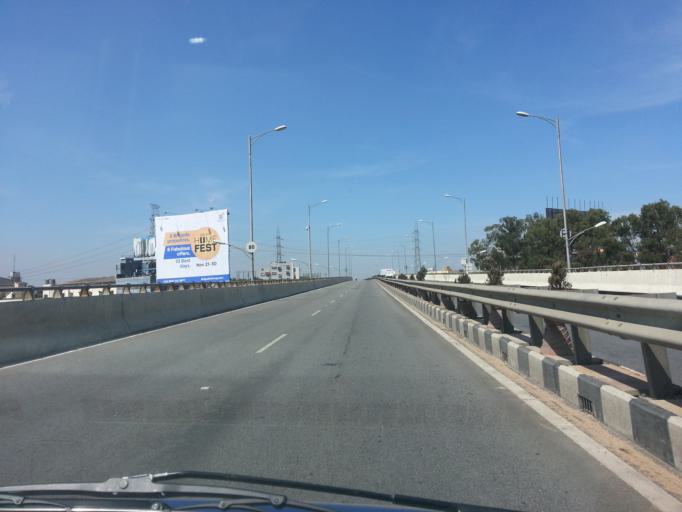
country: IN
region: Karnataka
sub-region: Bangalore Urban
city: Bangalore
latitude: 12.8714
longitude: 77.6521
